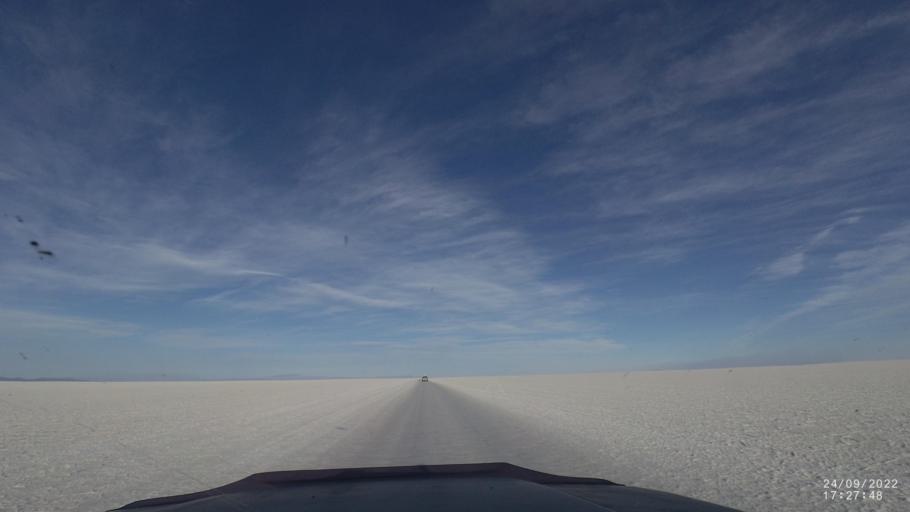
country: BO
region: Potosi
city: Colchani
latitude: -20.3009
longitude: -67.4410
